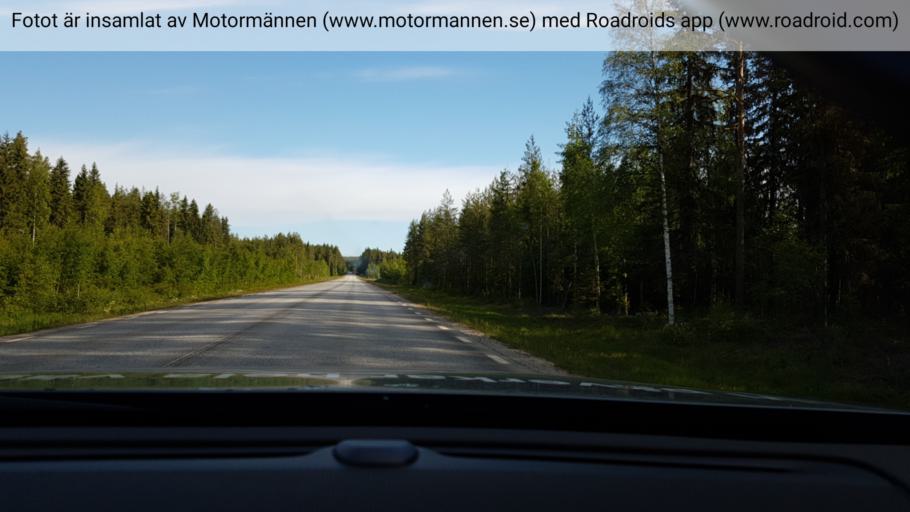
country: SE
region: Vaesterbotten
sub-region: Vannas Kommun
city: Vaennaes
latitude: 63.9497
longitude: 19.7583
